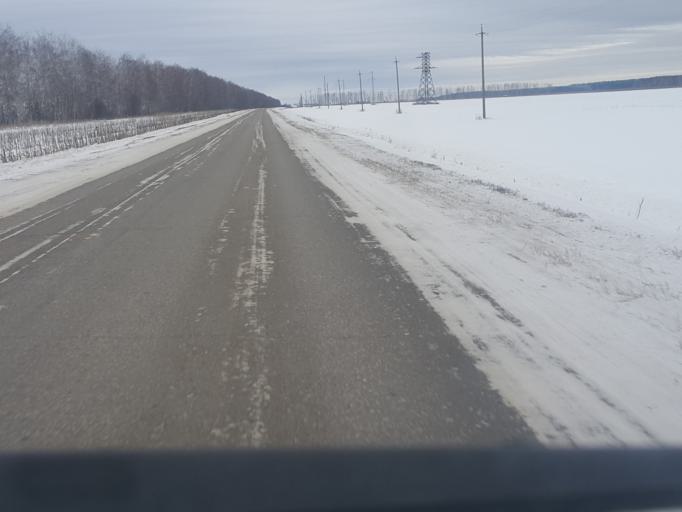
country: RU
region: Tambov
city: Rasskazovo
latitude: 52.8253
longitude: 41.8029
